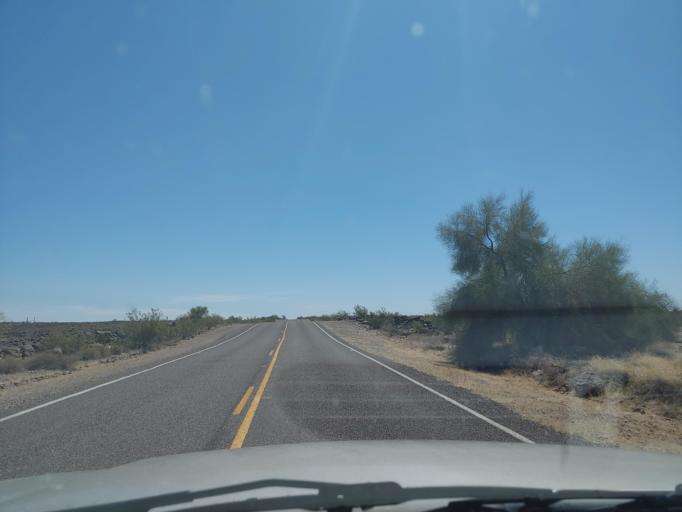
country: US
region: Arizona
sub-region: Maricopa County
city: Gila Bend
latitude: 32.9124
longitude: -113.2740
